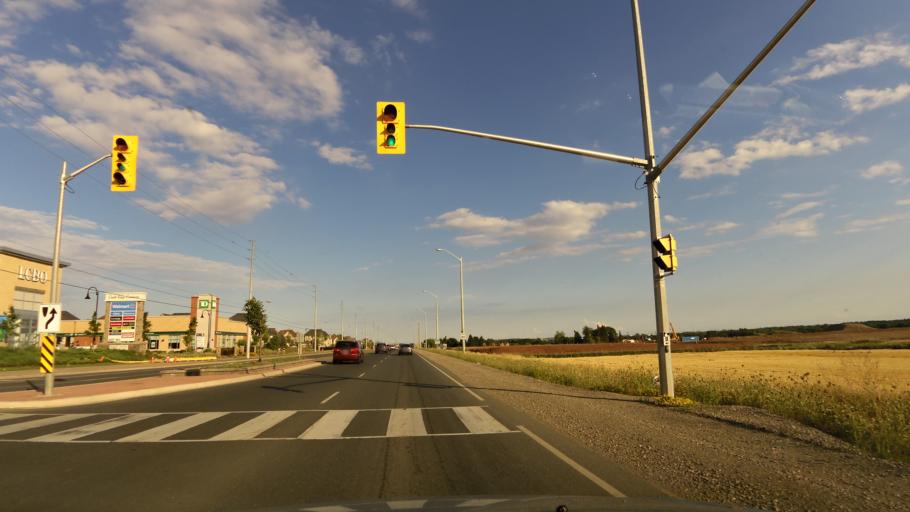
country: CA
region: Ontario
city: Brampton
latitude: 43.6562
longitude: -79.8150
